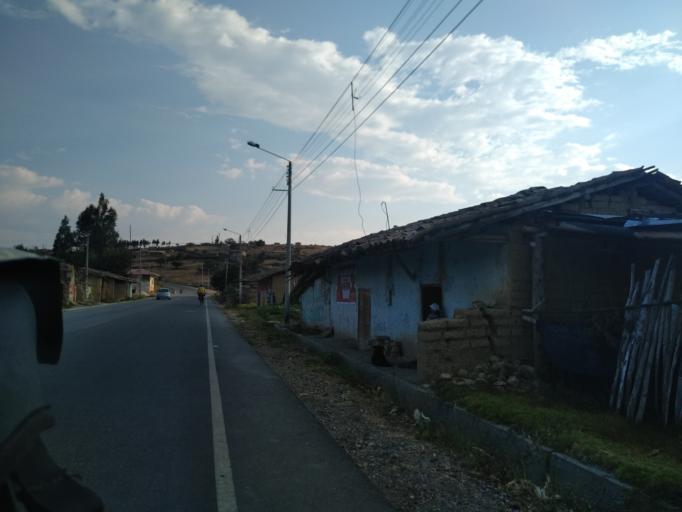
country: PE
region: Cajamarca
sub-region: San Marcos
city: La Grama
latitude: -7.3963
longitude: -78.1250
